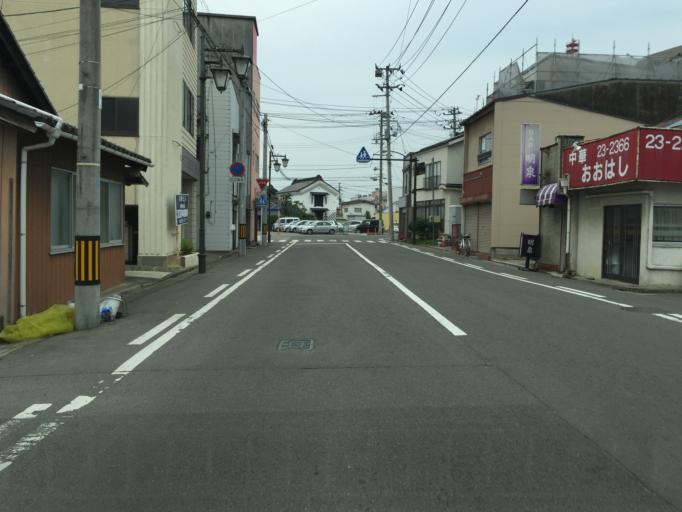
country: JP
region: Fukushima
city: Fukushima-shi
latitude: 37.7543
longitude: 140.4731
